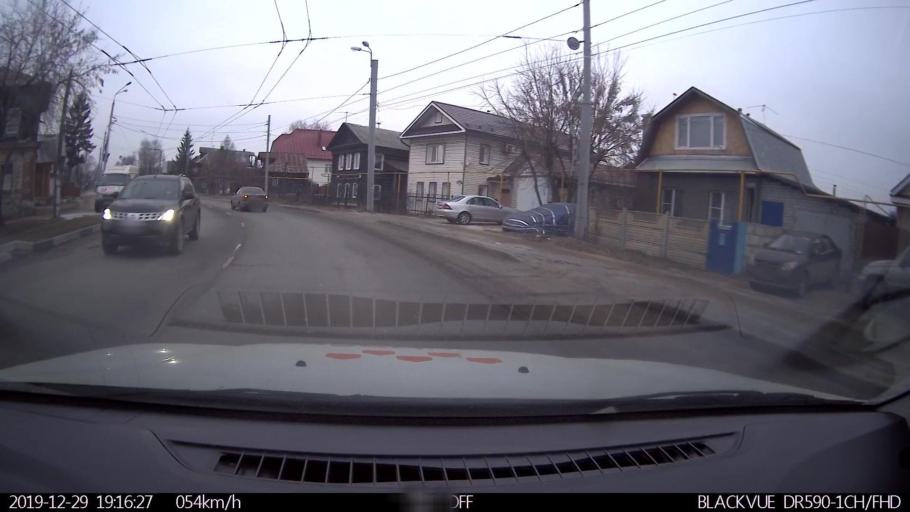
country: RU
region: Nizjnij Novgorod
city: Neklyudovo
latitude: 56.3805
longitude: 43.8311
